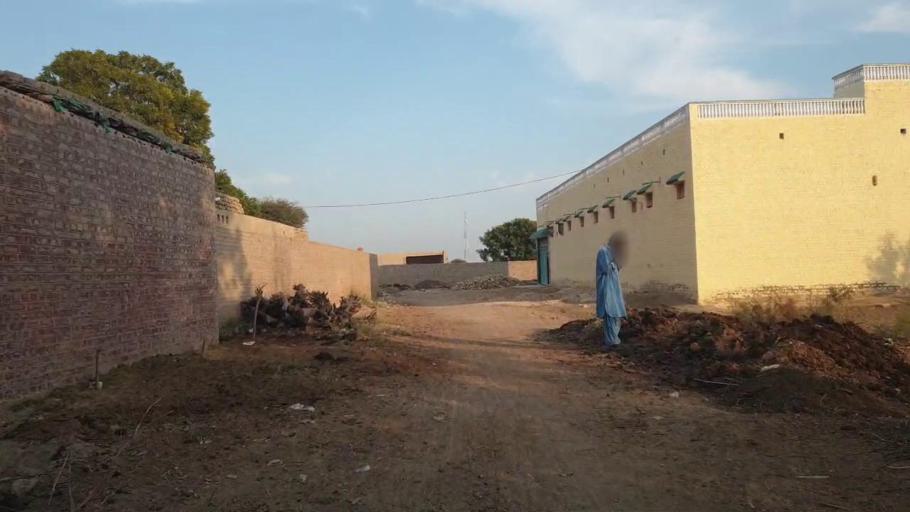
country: PK
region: Sindh
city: Shahpur Chakar
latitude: 26.1626
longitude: 68.6261
